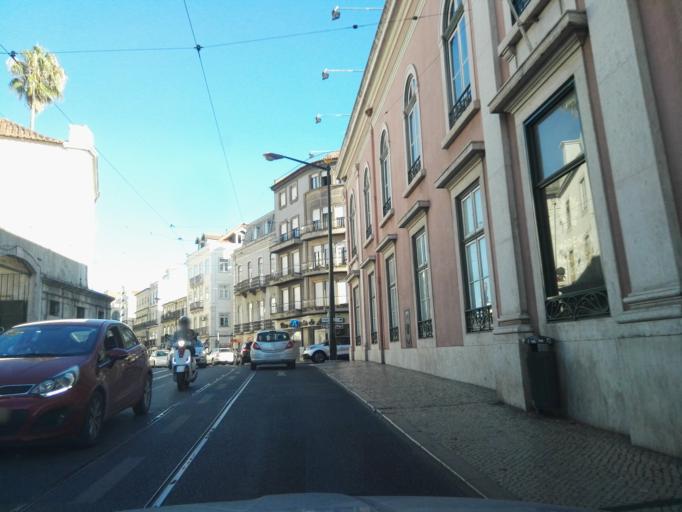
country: PT
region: Lisbon
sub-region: Lisbon
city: Lisbon
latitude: 38.7179
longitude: -9.1518
